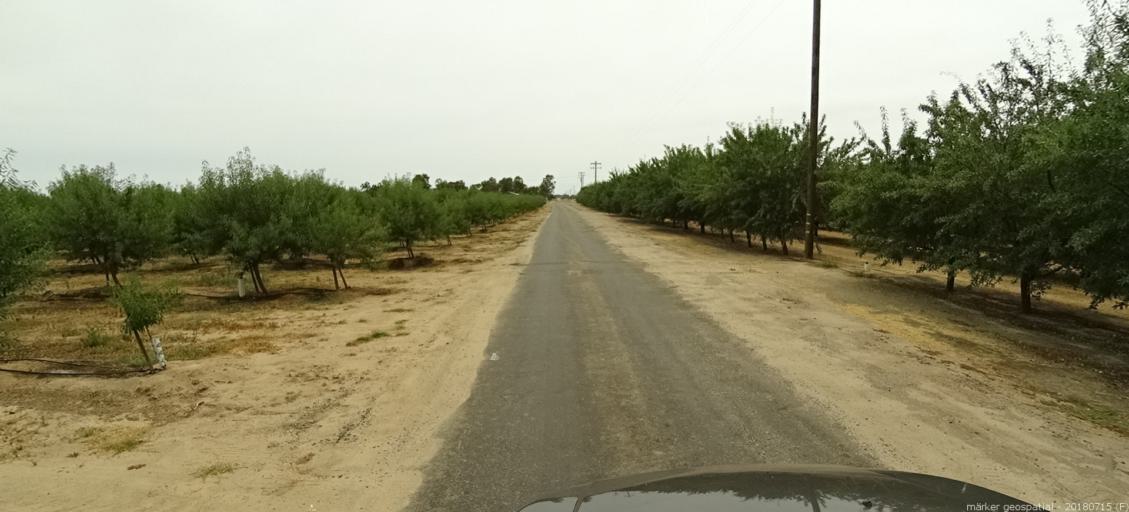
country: US
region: California
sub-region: Madera County
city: Madera Acres
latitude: 37.0255
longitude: -120.1132
